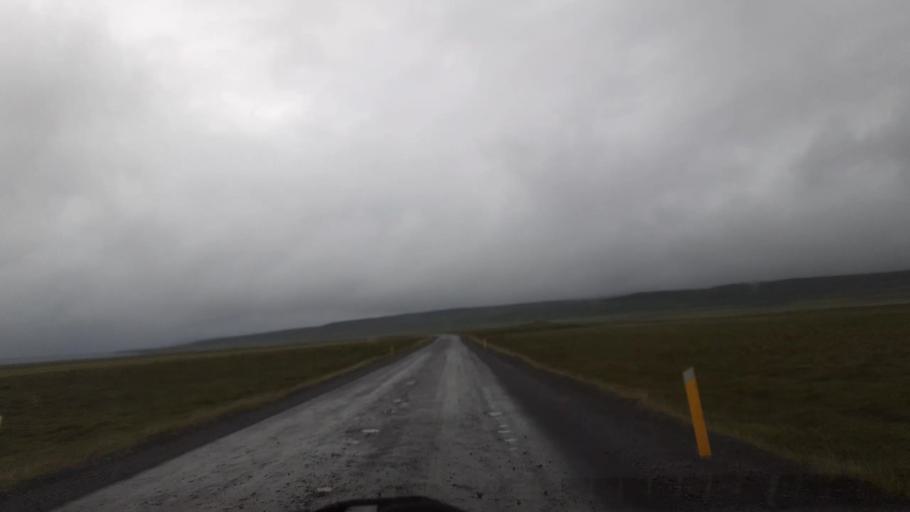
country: IS
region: East
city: Egilsstadir
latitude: 66.0343
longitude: -15.0607
